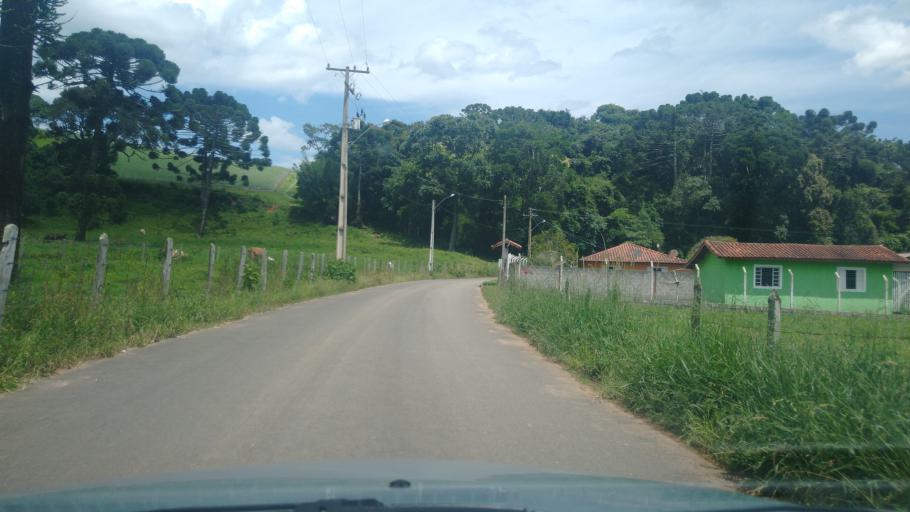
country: BR
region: Minas Gerais
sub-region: Extrema
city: Extrema
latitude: -22.7274
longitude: -46.3182
